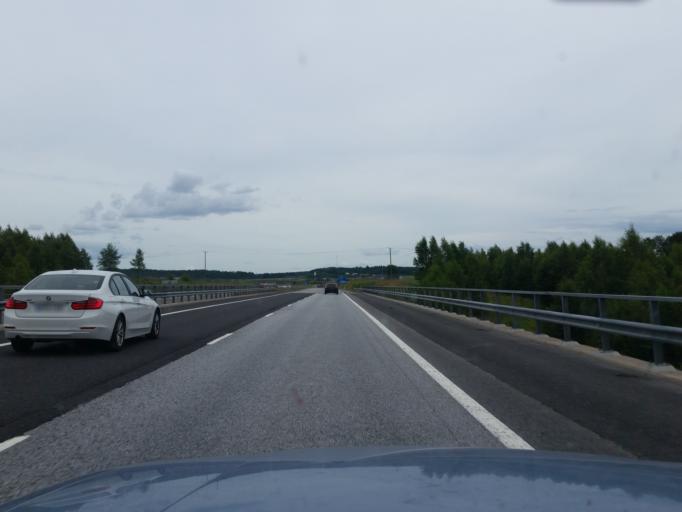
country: FI
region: Varsinais-Suomi
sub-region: Salo
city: Halikko
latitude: 60.4295
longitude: 23.0099
